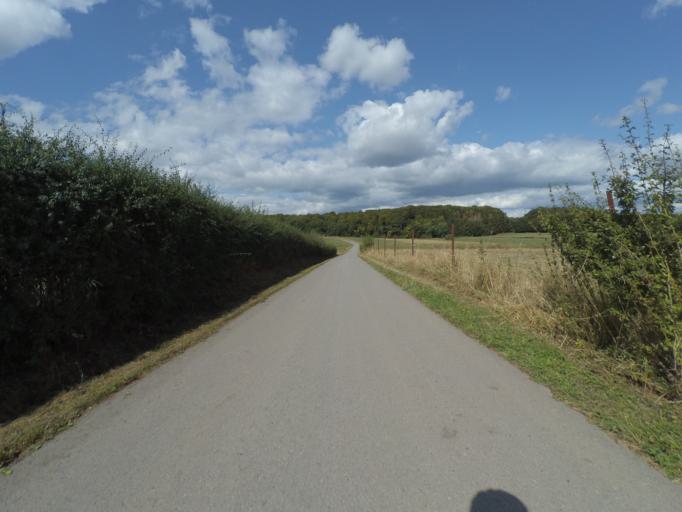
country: LU
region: Grevenmacher
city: Gonderange
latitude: 49.6823
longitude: 6.2657
